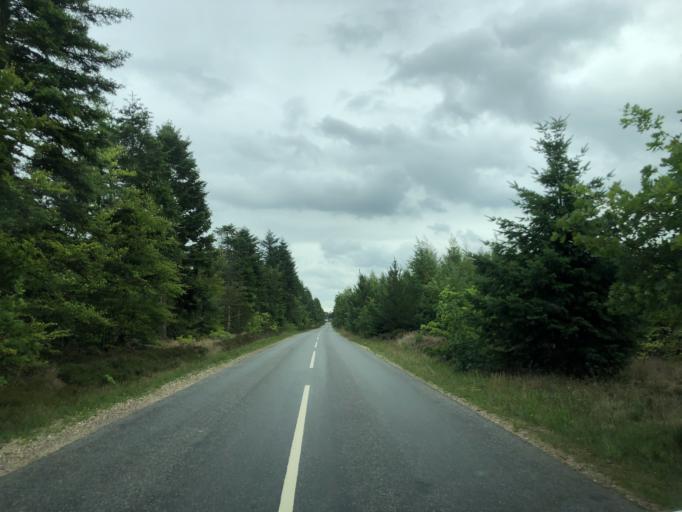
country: DK
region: Central Jutland
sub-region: Herning Kommune
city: Lind
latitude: 56.0883
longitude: 8.9696
